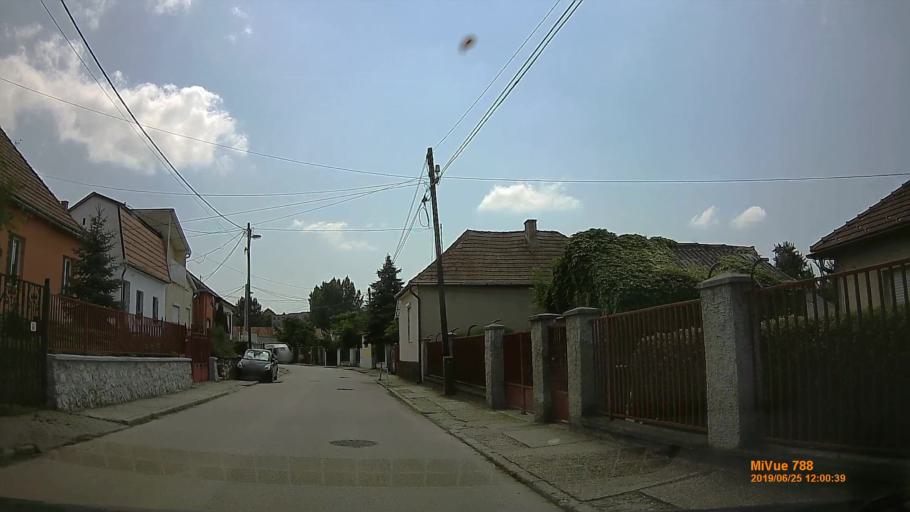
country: HU
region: Komarom-Esztergom
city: Dorog
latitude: 47.7264
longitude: 18.7369
